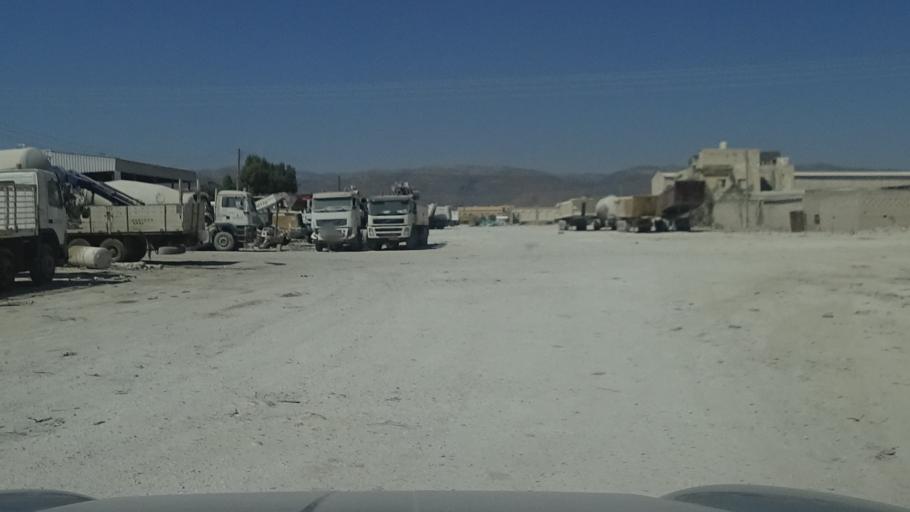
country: OM
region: Zufar
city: Salalah
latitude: 17.0283
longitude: 54.0425
